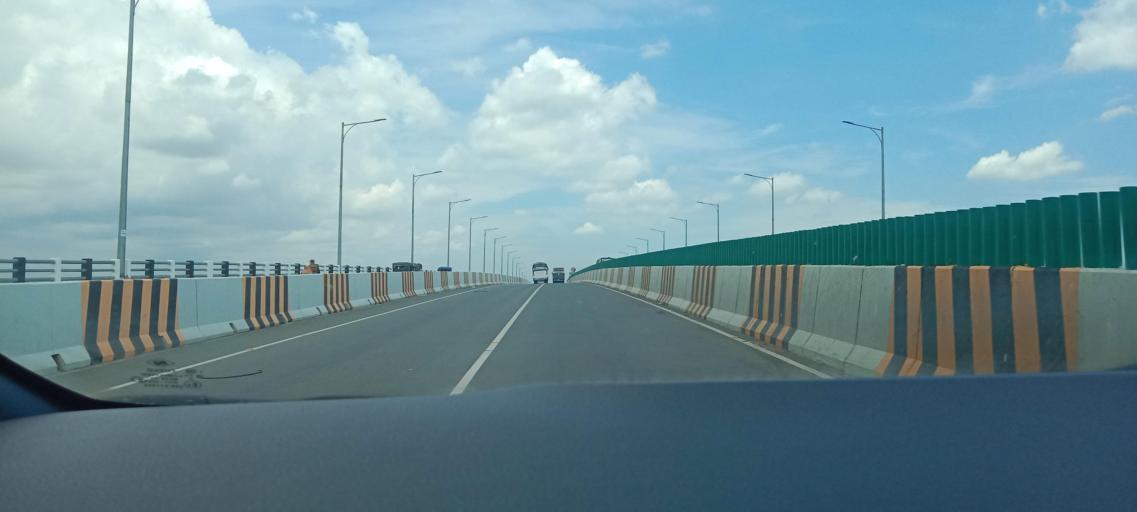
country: BD
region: Dhaka
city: Char Bhadrasan
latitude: 23.3851
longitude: 89.9955
